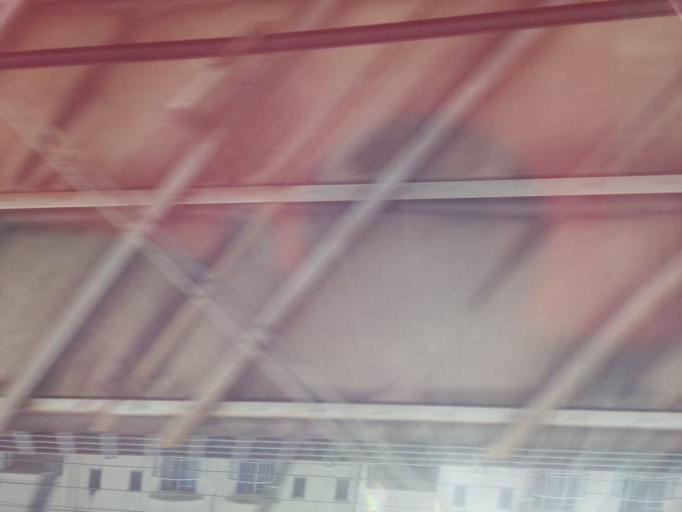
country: JP
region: Shiga Prefecture
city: Otsu-shi
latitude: 34.9712
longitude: 135.8963
